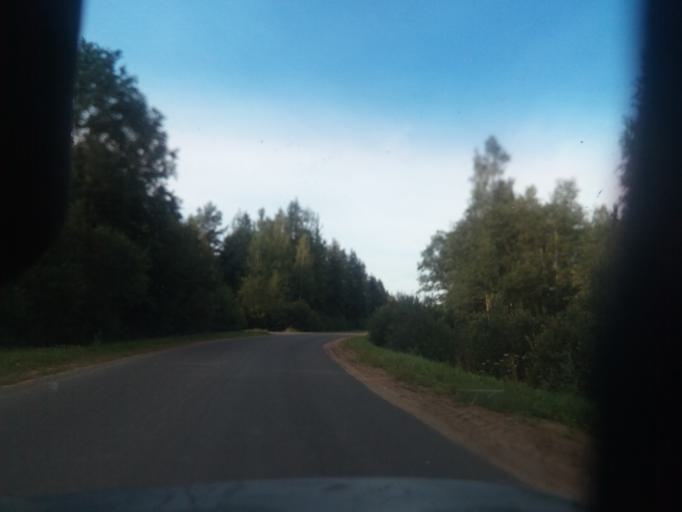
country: BY
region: Vitebsk
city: Dzisna
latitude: 55.6508
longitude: 28.3243
